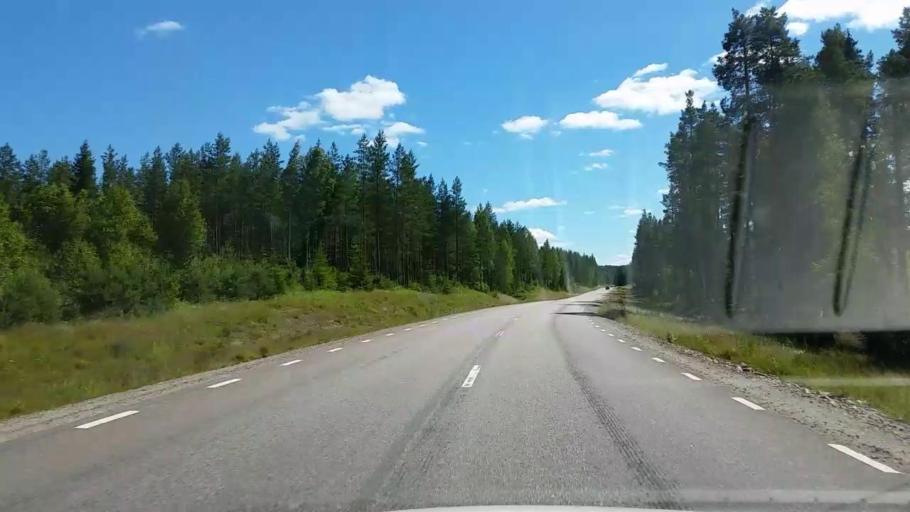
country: SE
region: Gaevleborg
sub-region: Ovanakers Kommun
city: Edsbyn
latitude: 61.1858
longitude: 15.8770
